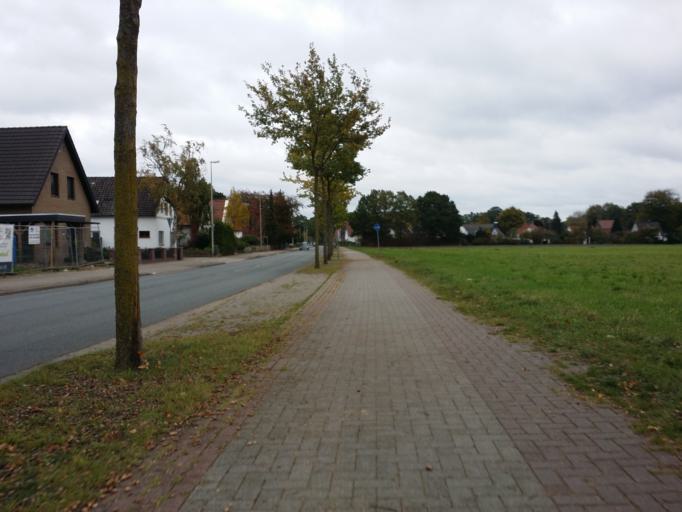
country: DE
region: Lower Saxony
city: Delmenhorst
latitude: 53.0500
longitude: 8.6770
